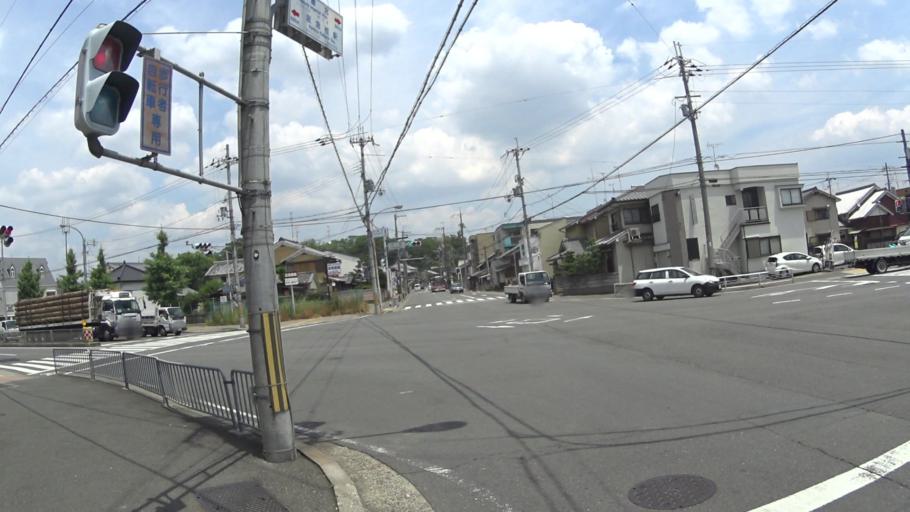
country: JP
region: Kyoto
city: Muko
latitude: 34.9811
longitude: 135.7089
